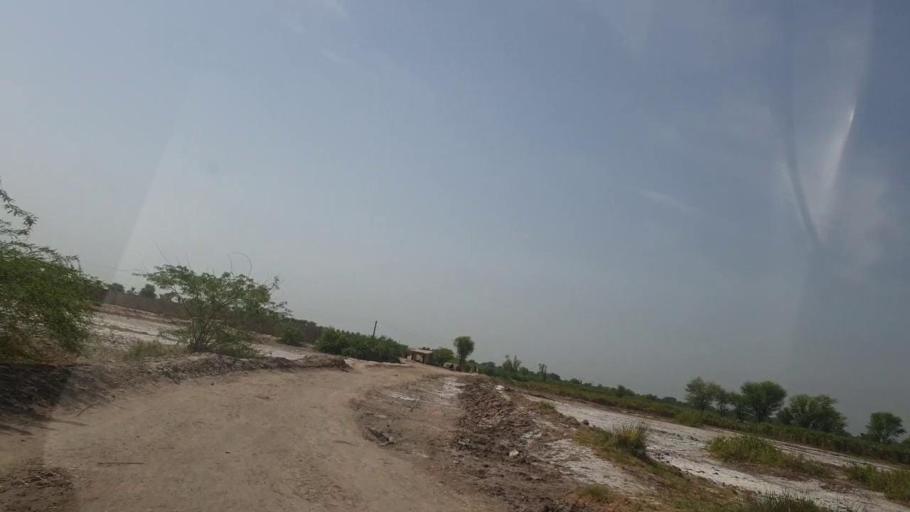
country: PK
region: Sindh
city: Gambat
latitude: 27.3797
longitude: 68.5833
